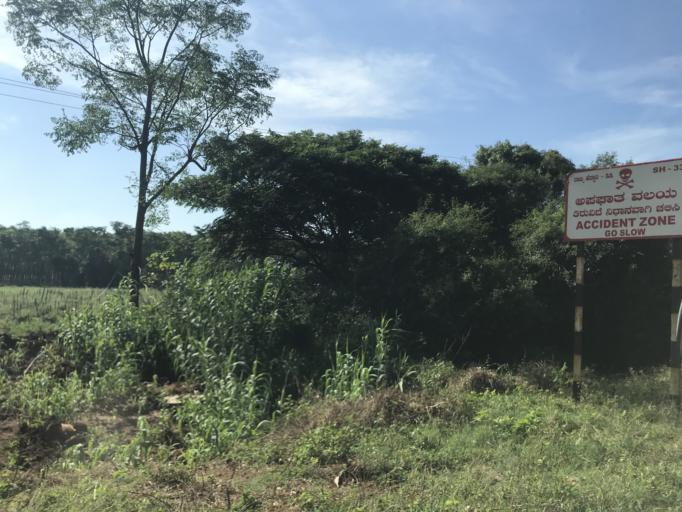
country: IN
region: Karnataka
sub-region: Mysore
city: Mysore
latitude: 12.2130
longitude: 76.5624
